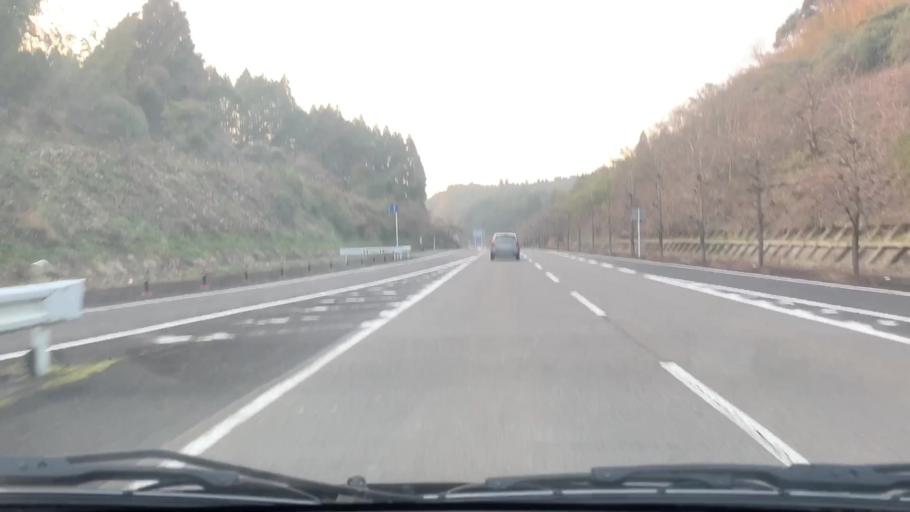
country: JP
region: Saga Prefecture
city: Imaricho-ko
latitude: 33.2652
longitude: 129.9576
